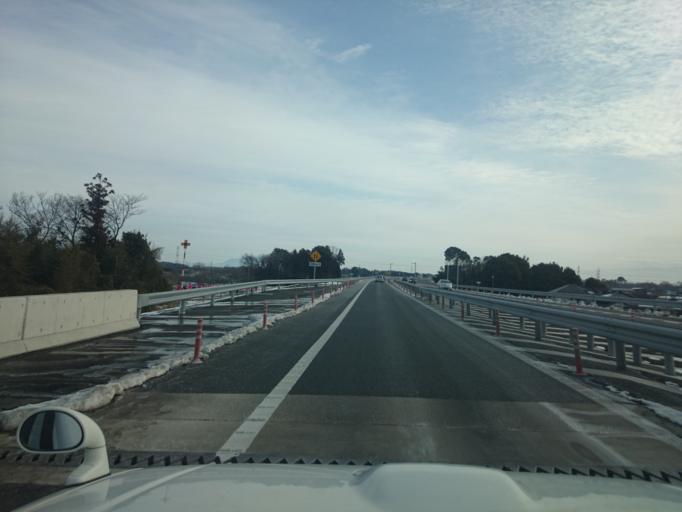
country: JP
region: Ibaraki
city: Sakai
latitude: 36.1246
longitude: 139.8181
